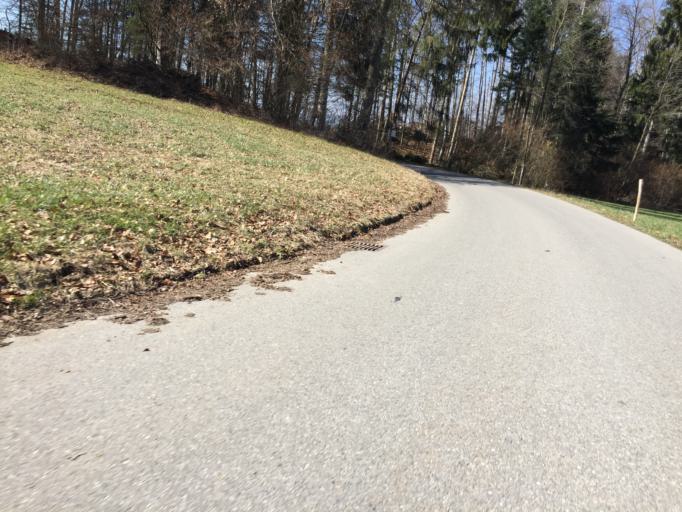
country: CH
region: Bern
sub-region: Bern-Mittelland District
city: Taegertschi
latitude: 46.9024
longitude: 7.5868
